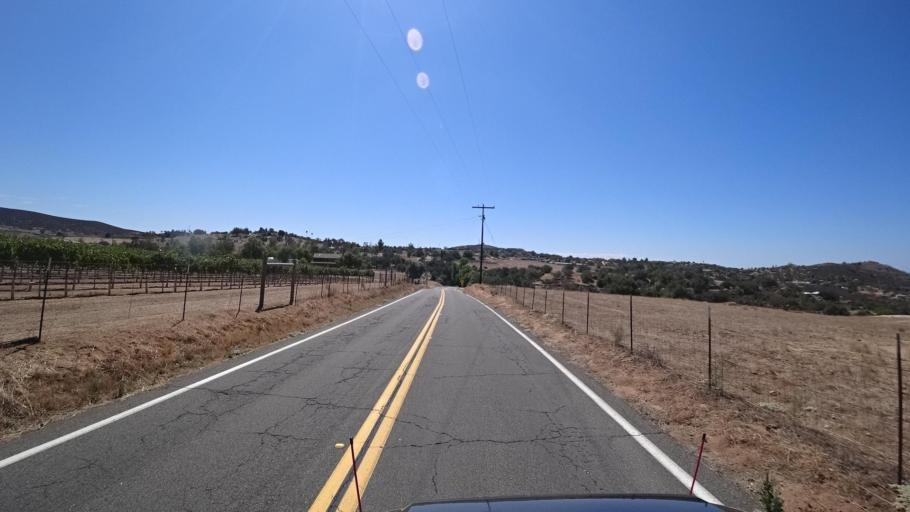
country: US
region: California
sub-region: San Diego County
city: Ramona
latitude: 33.0435
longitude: -116.8239
